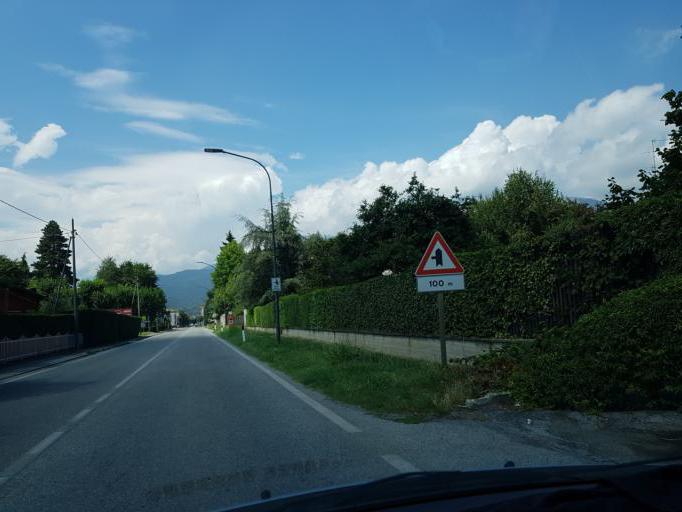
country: IT
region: Piedmont
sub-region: Provincia di Cuneo
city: Dronero
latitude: 44.4598
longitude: 7.3744
